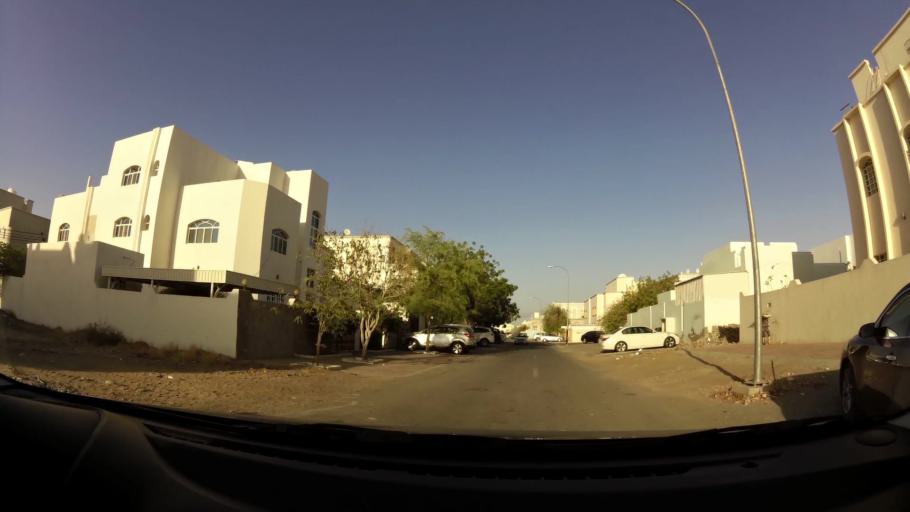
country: OM
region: Muhafazat Masqat
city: As Sib al Jadidah
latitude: 23.6106
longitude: 58.2278
